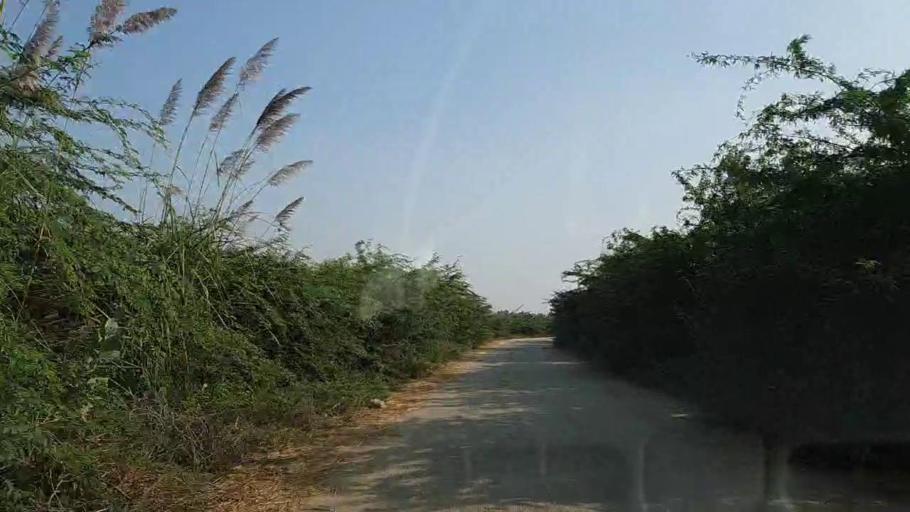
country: PK
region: Sindh
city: Mirpur Sakro
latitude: 24.6207
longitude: 67.6591
